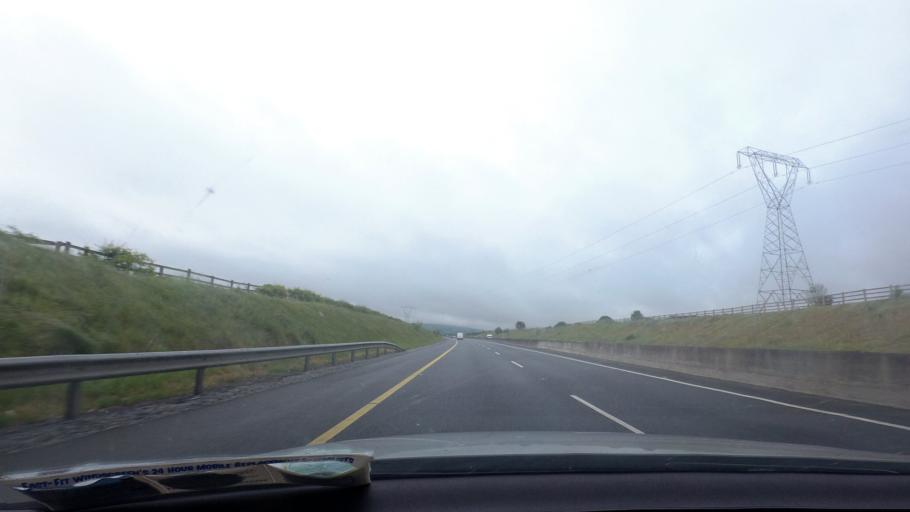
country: IE
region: Munster
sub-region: North Tipperary
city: Nenagh
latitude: 52.8256
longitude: -8.3001
